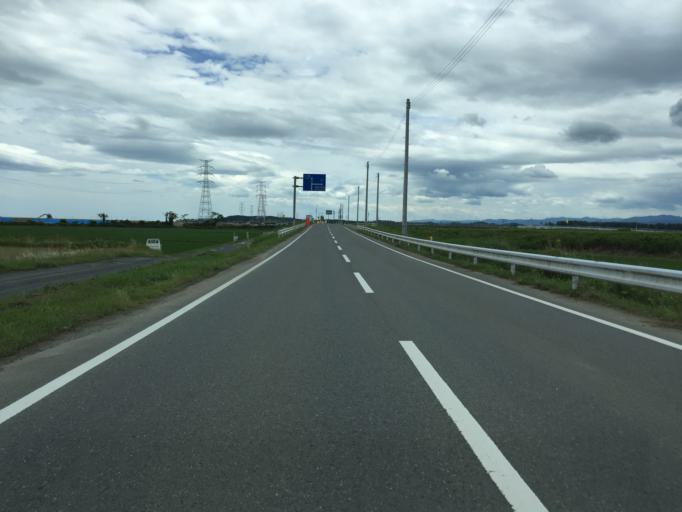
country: JP
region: Fukushima
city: Namie
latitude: 37.6472
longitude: 141.0153
